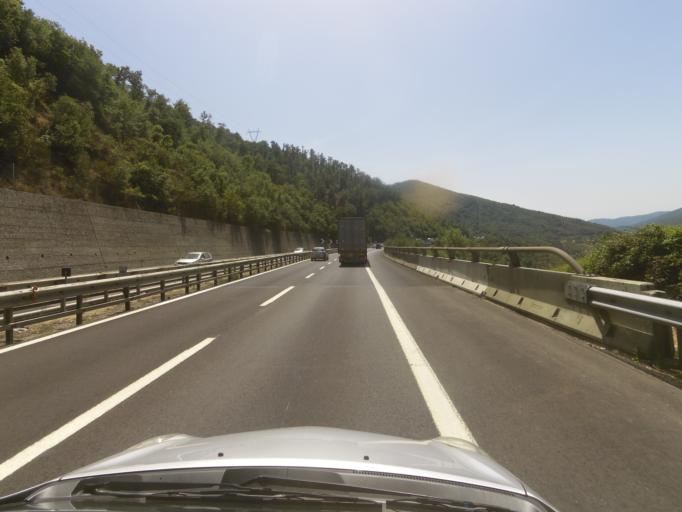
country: IT
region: Tuscany
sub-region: Province of Florence
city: Carraia
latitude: 43.9282
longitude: 11.2181
